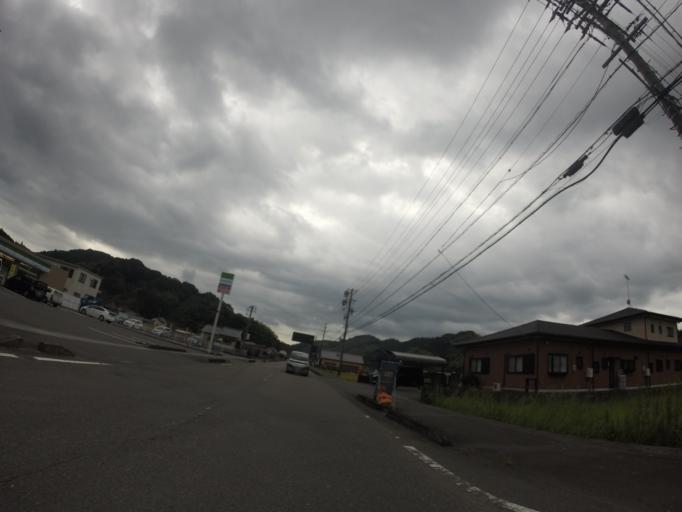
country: JP
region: Shizuoka
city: Fujieda
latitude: 34.9087
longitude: 138.2630
